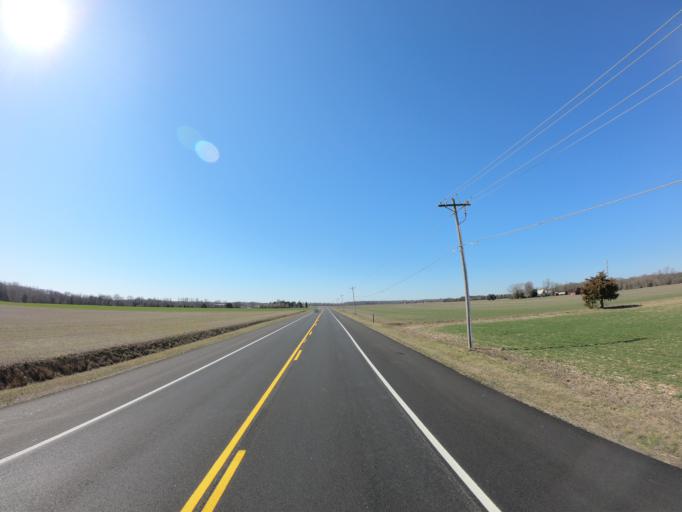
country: US
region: Delaware
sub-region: New Castle County
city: Townsend
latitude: 39.3628
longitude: -75.8236
